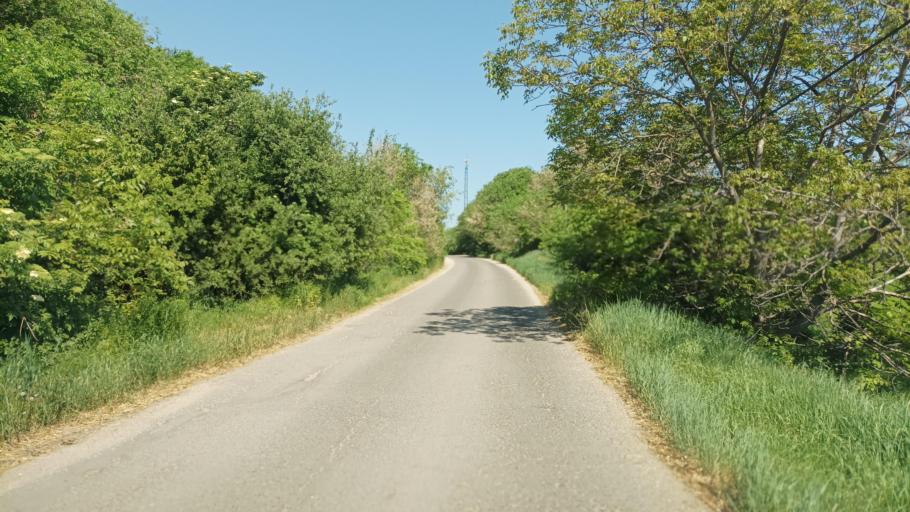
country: HU
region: Pest
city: Uri
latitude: 47.3935
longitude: 19.4970
